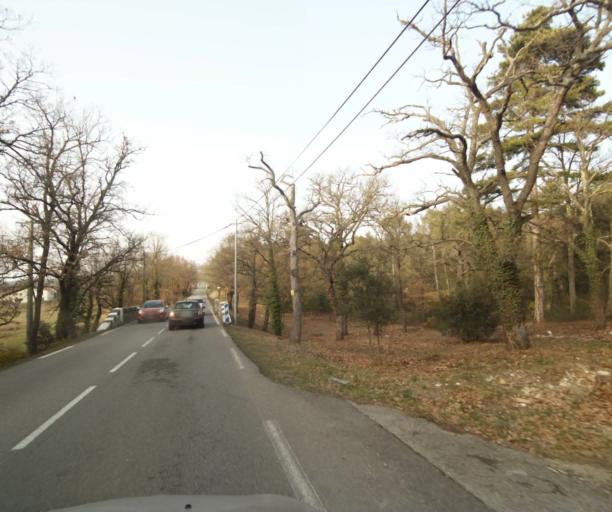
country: FR
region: Provence-Alpes-Cote d'Azur
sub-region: Departement des Bouches-du-Rhone
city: Eguilles
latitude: 43.5983
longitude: 5.3663
